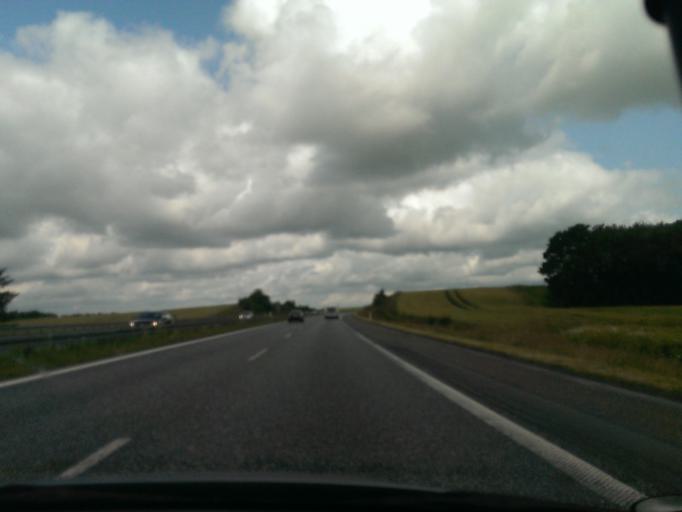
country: DK
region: North Denmark
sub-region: Mariagerfjord Kommune
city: Mariager
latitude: 56.5451
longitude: 9.8910
